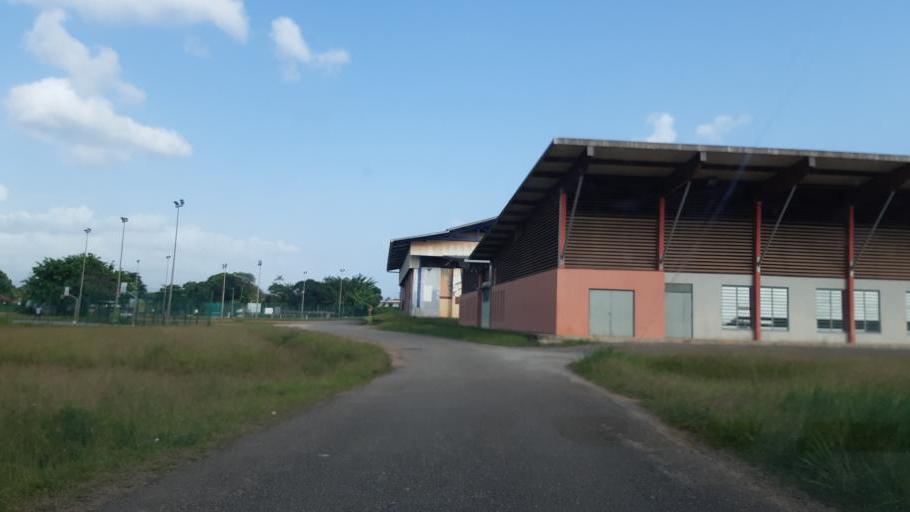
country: GF
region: Guyane
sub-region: Guyane
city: Matoury
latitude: 4.8476
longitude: -52.3284
